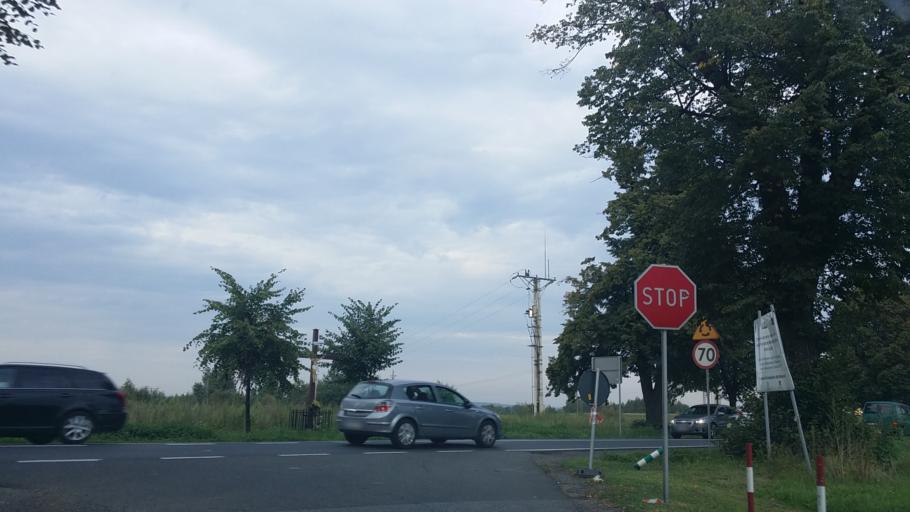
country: PL
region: Lesser Poland Voivodeship
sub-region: Powiat oswiecimski
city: Zator
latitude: 49.9988
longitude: 19.4175
